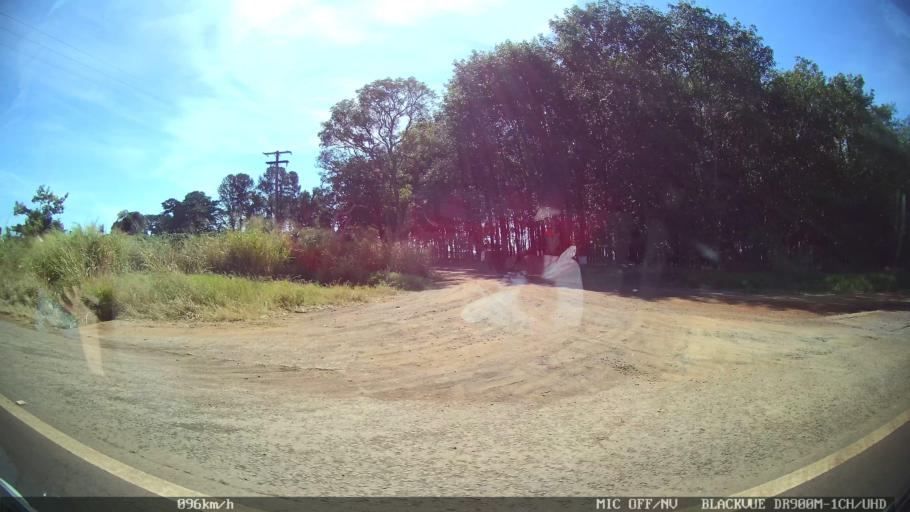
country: BR
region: Sao Paulo
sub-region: Franca
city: Franca
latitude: -20.5582
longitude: -47.5486
